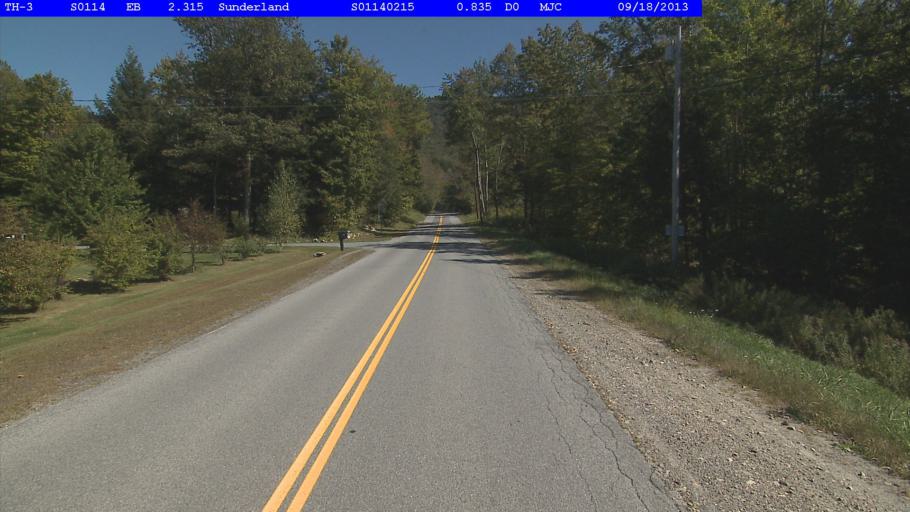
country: US
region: Vermont
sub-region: Bennington County
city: Arlington
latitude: 43.0580
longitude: -73.1223
